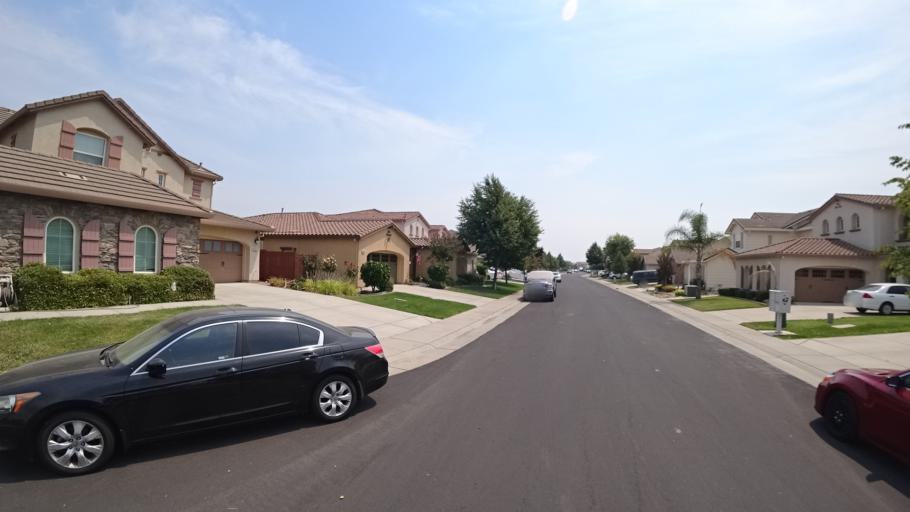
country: US
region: California
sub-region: Sacramento County
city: Laguna
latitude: 38.4008
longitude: -121.4049
